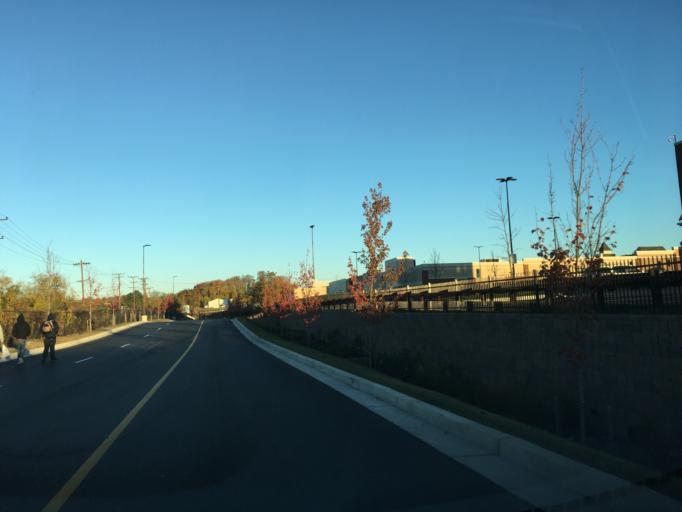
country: US
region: Maryland
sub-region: Baltimore County
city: Owings Mills
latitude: 39.4115
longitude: -76.7741
